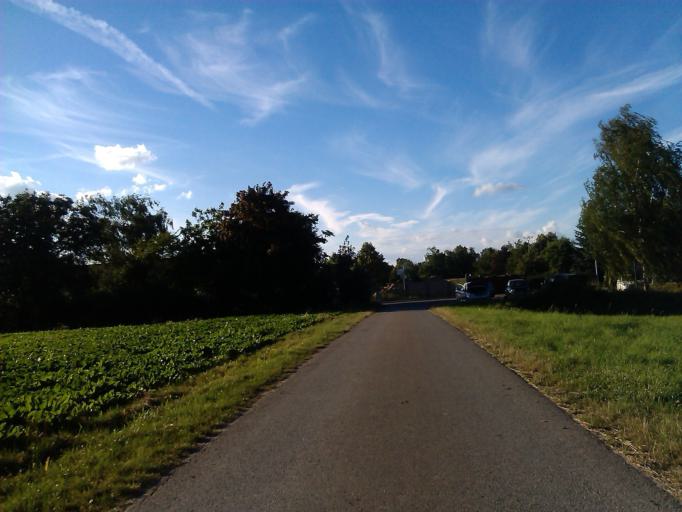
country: DE
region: Rheinland-Pfalz
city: Otterstadt
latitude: 49.3712
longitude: 8.4609
